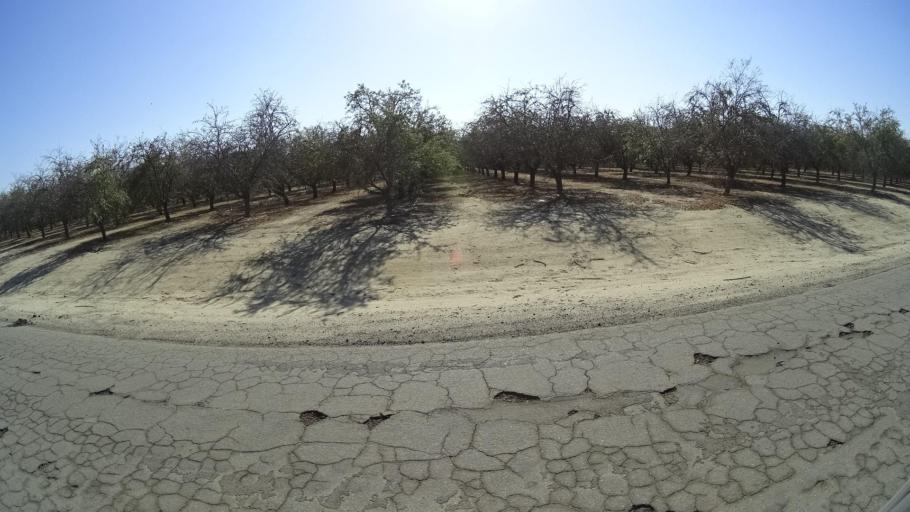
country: US
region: California
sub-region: Kern County
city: McFarland
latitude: 35.7035
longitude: -119.1573
